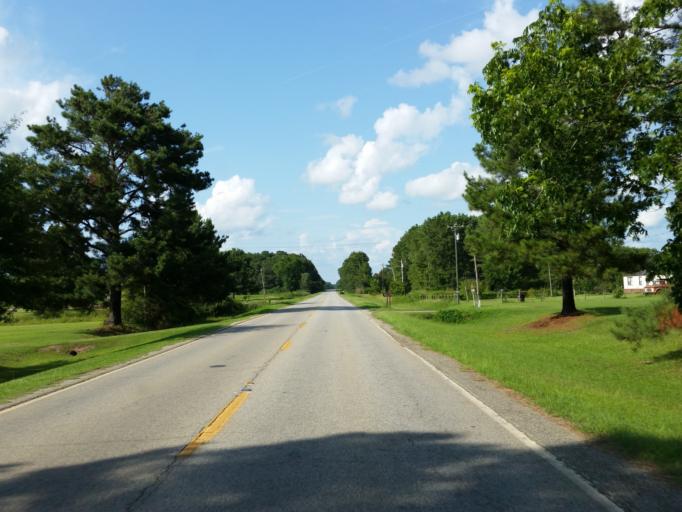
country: US
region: Georgia
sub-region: Lee County
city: Leesburg
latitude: 31.8264
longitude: -84.1050
